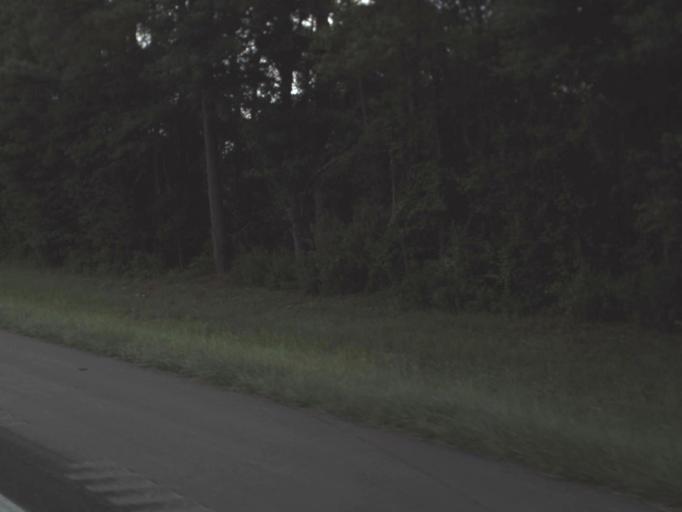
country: US
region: Georgia
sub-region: Echols County
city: Statenville
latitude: 30.5844
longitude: -83.1101
